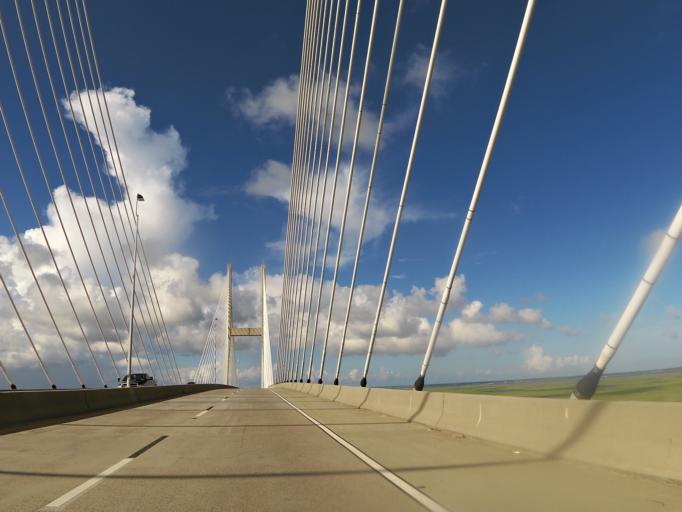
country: US
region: Georgia
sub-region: Glynn County
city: Brunswick
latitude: 31.1152
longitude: -81.4855
